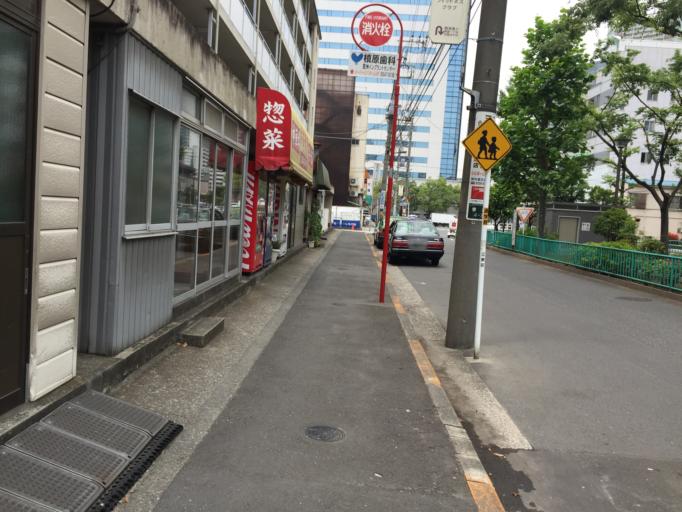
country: JP
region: Tokyo
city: Urayasu
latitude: 35.6546
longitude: 139.7986
